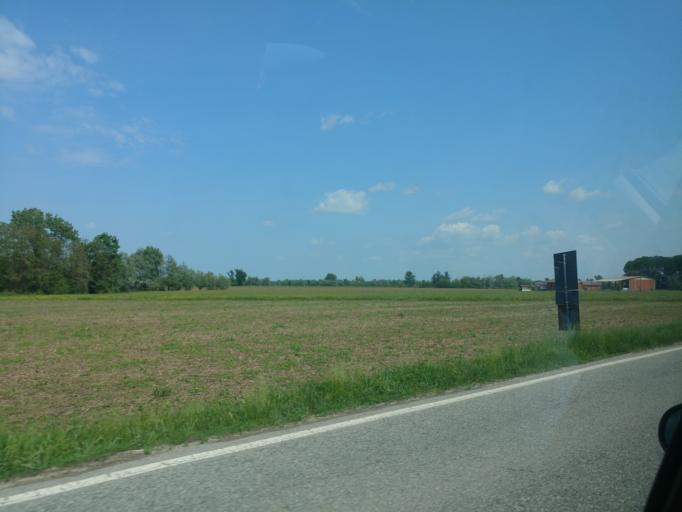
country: IT
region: Piedmont
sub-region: Provincia di Cuneo
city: Carde
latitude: 44.7302
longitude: 7.4274
